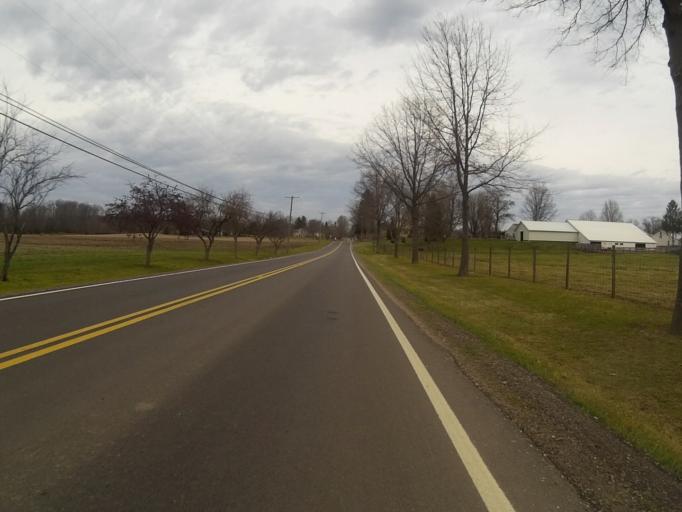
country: US
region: Ohio
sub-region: Portage County
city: Brimfield
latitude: 41.0717
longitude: -81.3286
